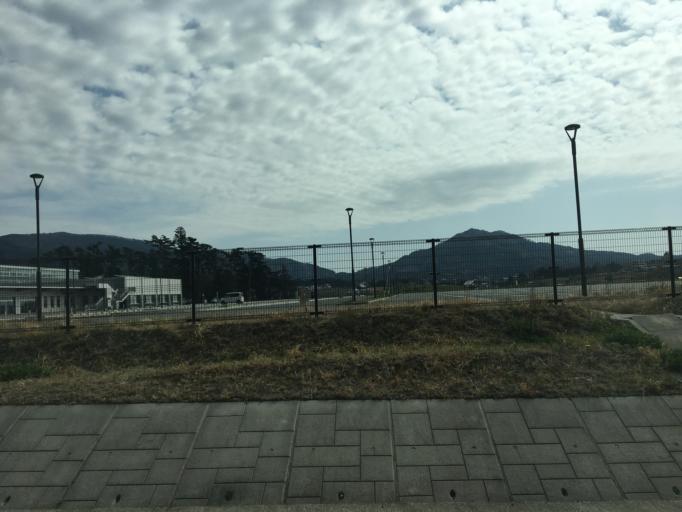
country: JP
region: Iwate
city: Ofunato
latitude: 39.0167
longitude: 141.6403
